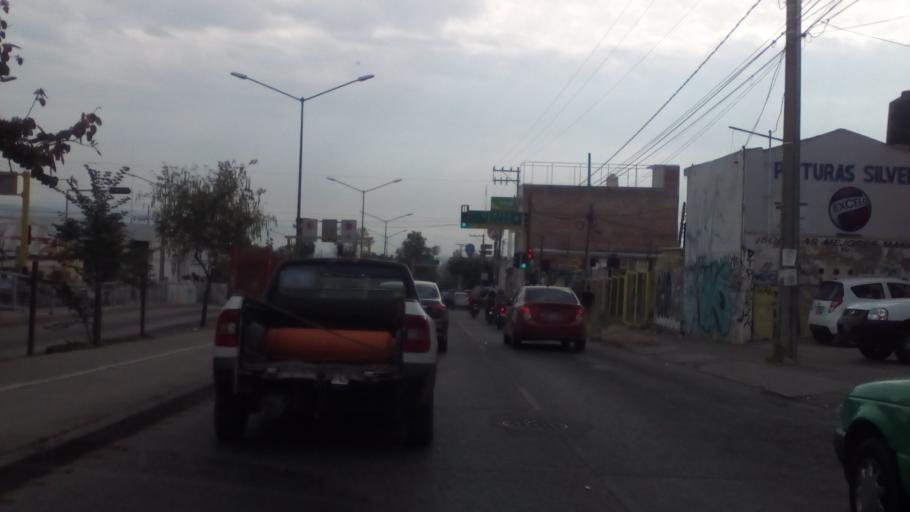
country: MX
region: Guanajuato
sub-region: Leon
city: La Ermita
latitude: 21.1325
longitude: -101.7124
